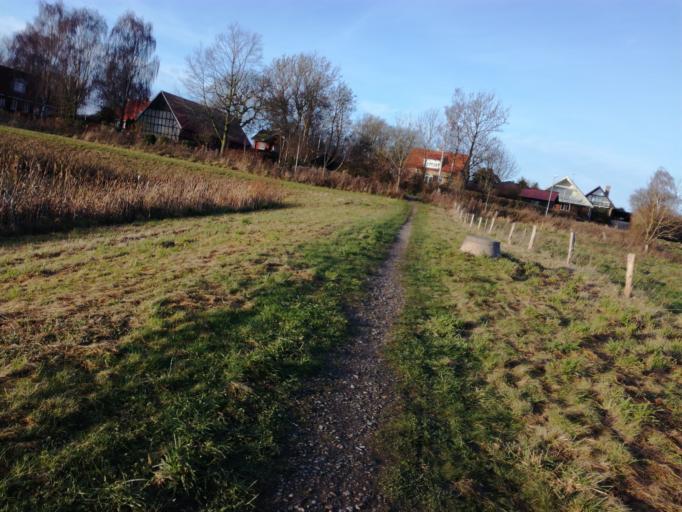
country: DK
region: South Denmark
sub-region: Fredericia Kommune
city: Fredericia
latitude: 55.6223
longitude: 9.7852
